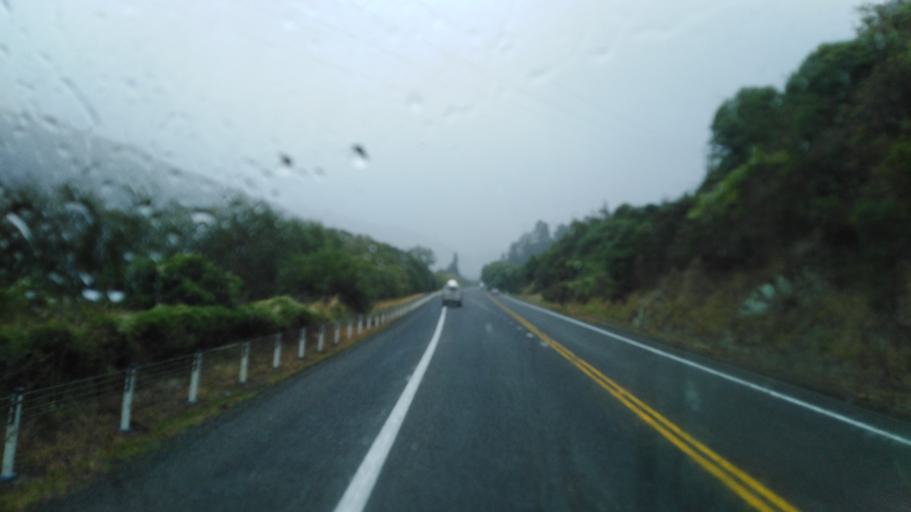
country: NZ
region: Marlborough
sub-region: Marlborough District
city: Picton
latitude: -41.3843
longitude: 173.9509
